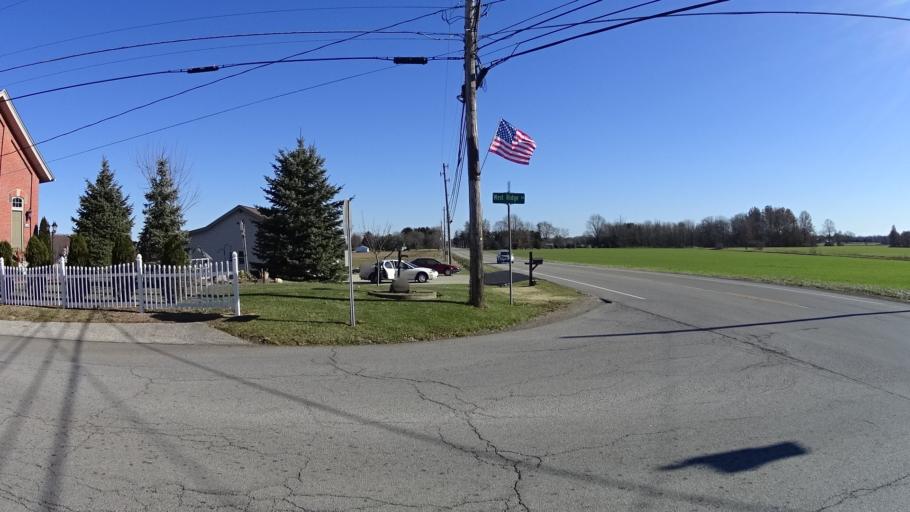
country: US
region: Ohio
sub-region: Lorain County
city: Elyria
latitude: 41.3367
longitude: -82.1514
